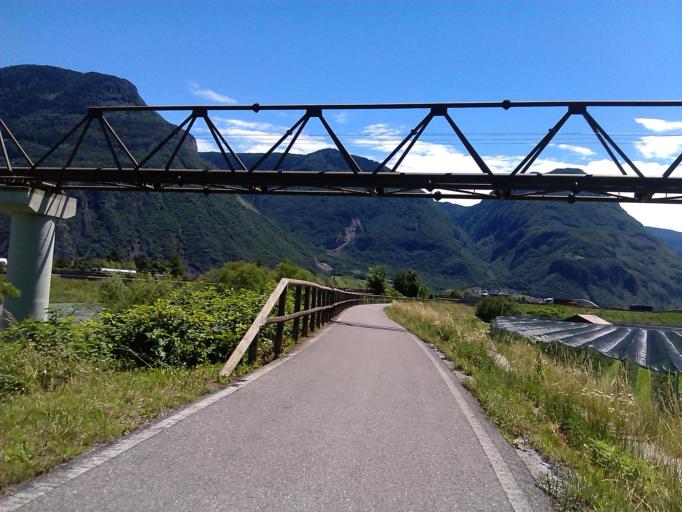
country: IT
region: Trentino-Alto Adige
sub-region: Bolzano
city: Vadena
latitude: 46.4231
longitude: 11.3111
